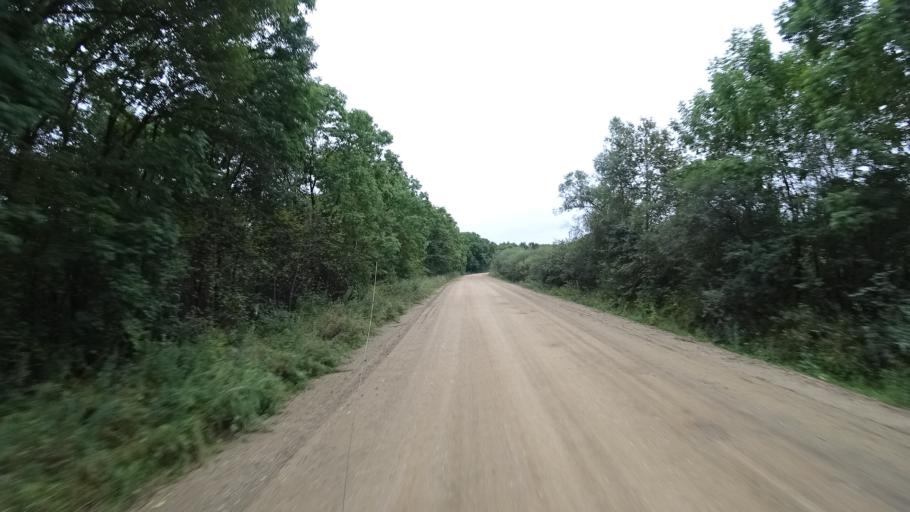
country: RU
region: Primorskiy
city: Rettikhovka
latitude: 44.1799
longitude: 132.8517
